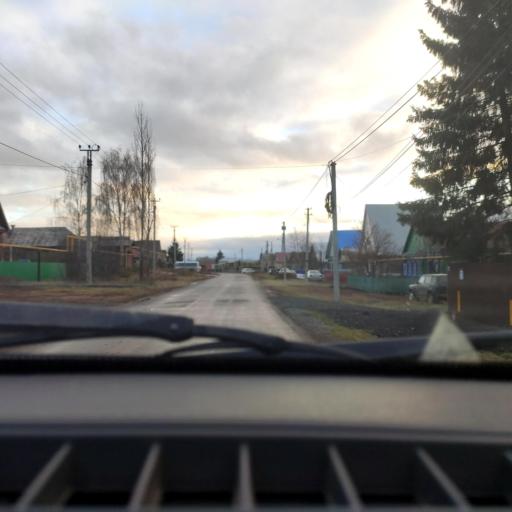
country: RU
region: Bashkortostan
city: Avdon
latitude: 54.6404
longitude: 55.7370
